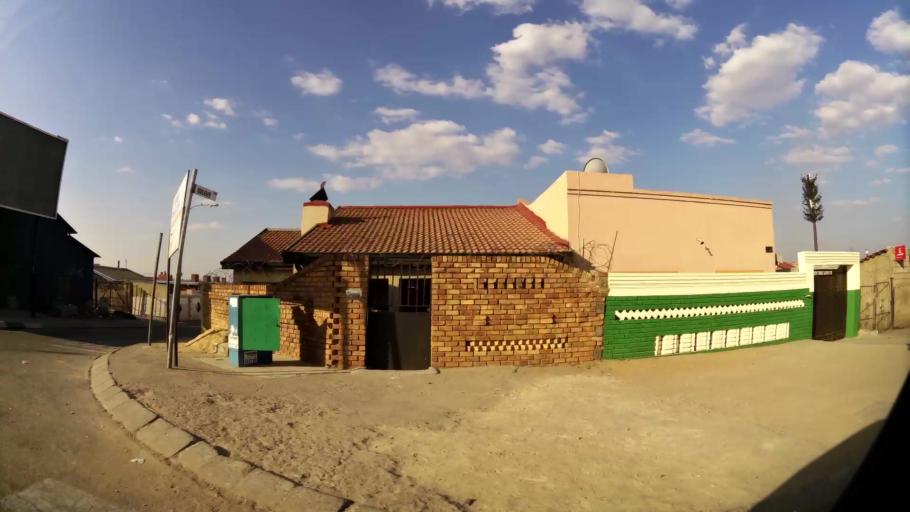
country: ZA
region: Gauteng
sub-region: City of Johannesburg Metropolitan Municipality
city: Soweto
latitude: -26.2301
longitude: 27.9006
